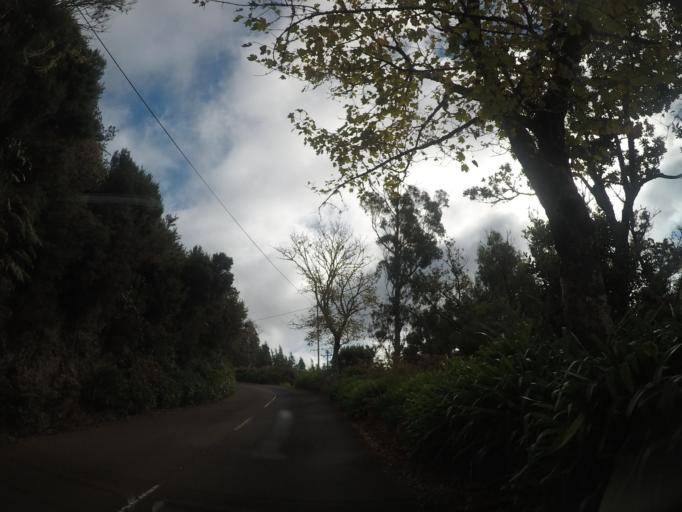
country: PT
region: Madeira
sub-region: Porto Moniz
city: Porto Moniz
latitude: 32.8366
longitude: -17.2124
